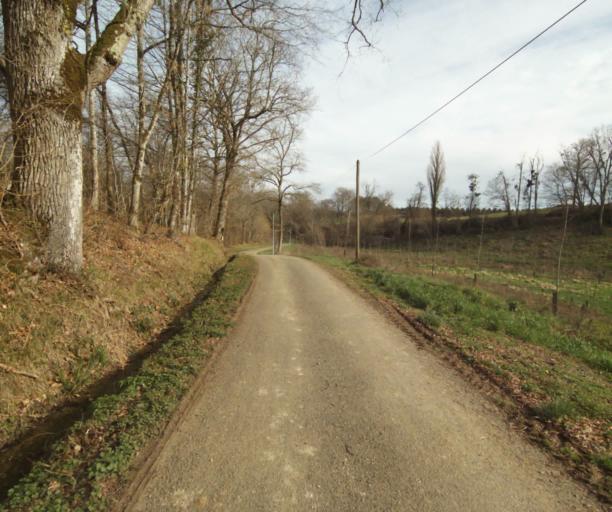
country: FR
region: Aquitaine
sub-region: Departement des Landes
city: Gabarret
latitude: 43.9659
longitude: 0.0493
